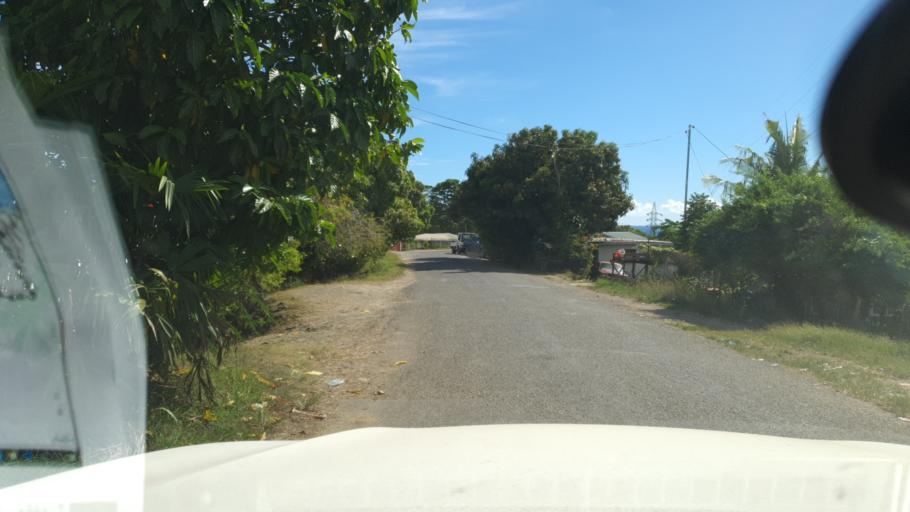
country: SB
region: Guadalcanal
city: Honiara
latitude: -9.4367
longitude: 159.9517
